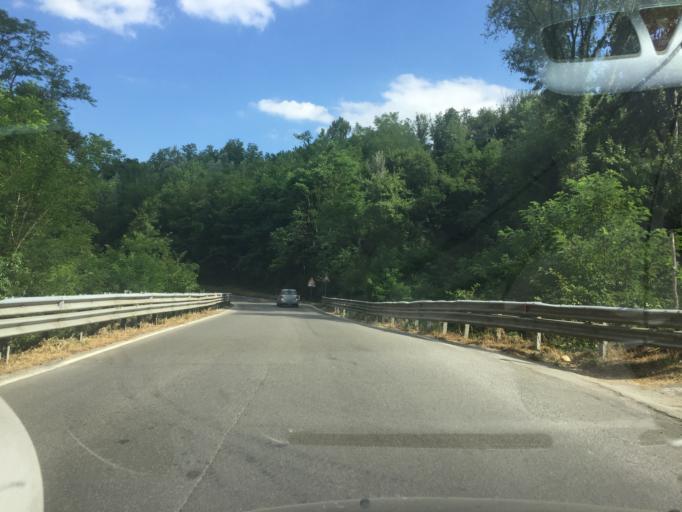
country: IT
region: Tuscany
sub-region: Provincia di Lucca
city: Castelnuovo di Garfagnana
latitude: 44.1253
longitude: 10.3871
